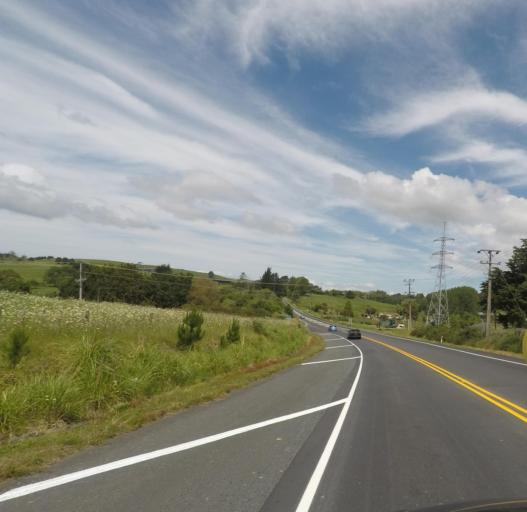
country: NZ
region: Auckland
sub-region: Auckland
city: Rothesay Bay
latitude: -36.6604
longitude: 174.6716
